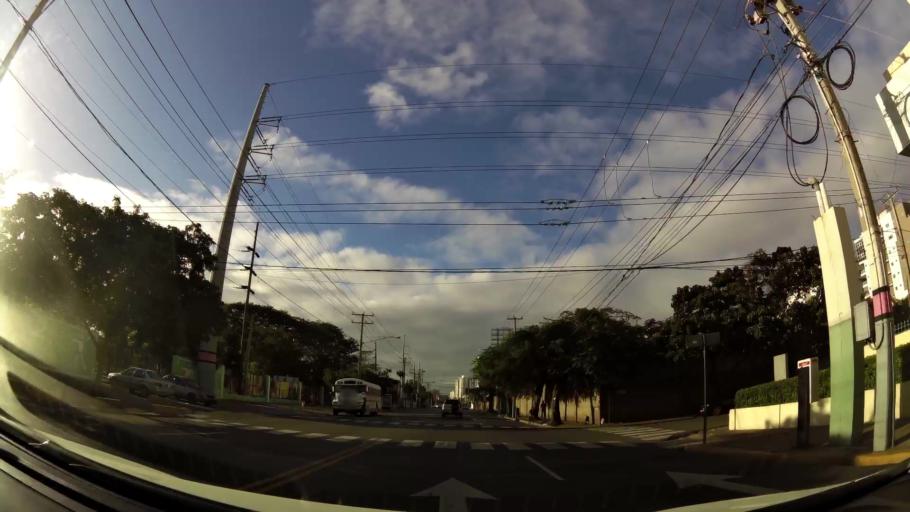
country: DO
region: Nacional
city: La Julia
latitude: 18.4807
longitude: -69.9207
